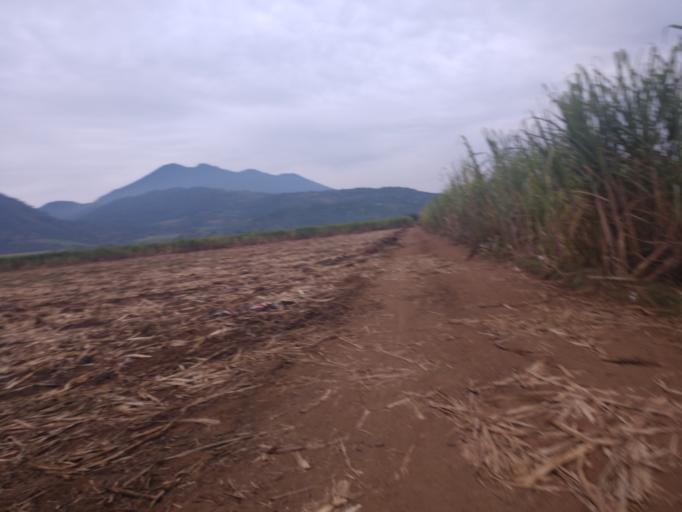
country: MX
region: Nayarit
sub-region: Tepic
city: La Corregidora
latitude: 21.4762
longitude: -104.8084
